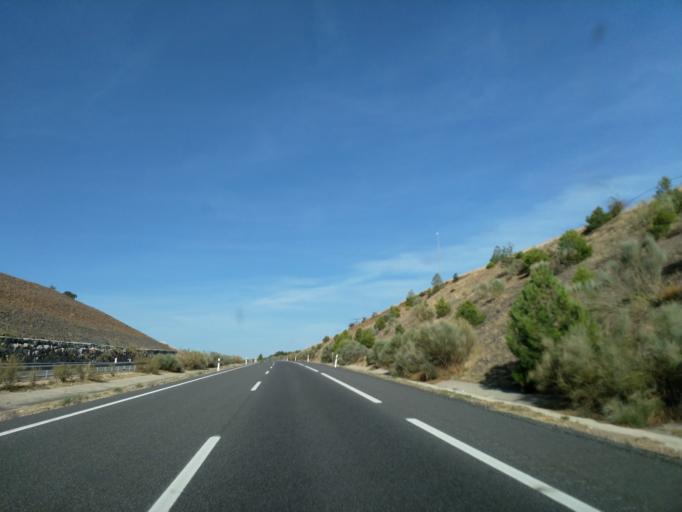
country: ES
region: Castille and Leon
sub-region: Provincia de Avila
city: Ojos-Albos
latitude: 40.7351
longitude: -4.5003
